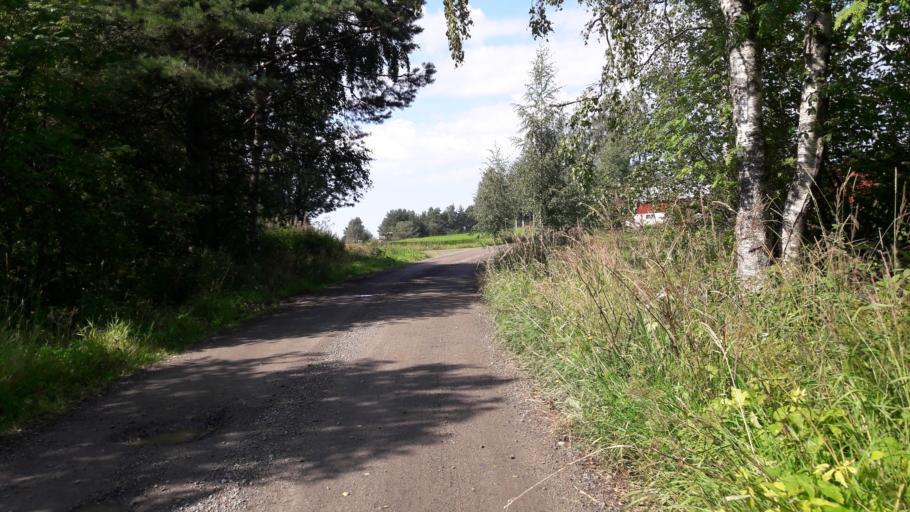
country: FI
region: North Karelia
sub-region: Joensuu
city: Joensuu
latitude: 62.5317
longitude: 29.8361
